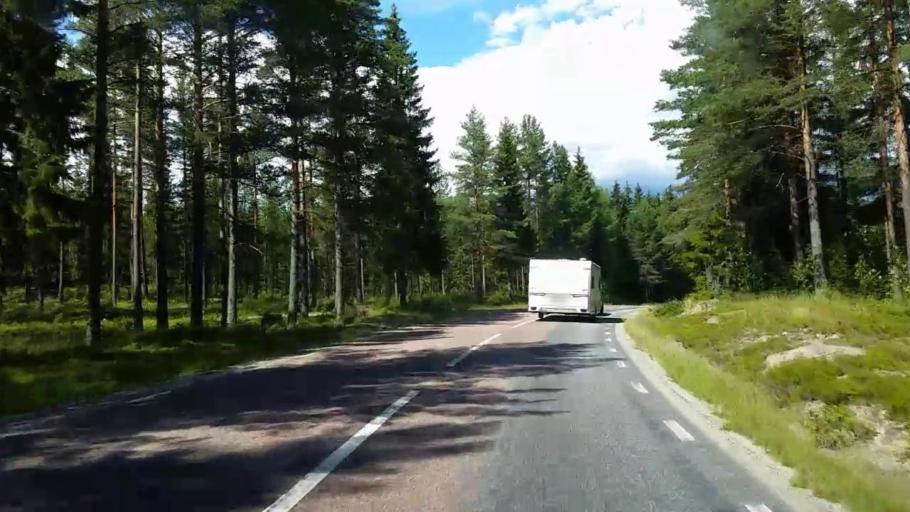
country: SE
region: Gaevleborg
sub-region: Ovanakers Kommun
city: Edsbyn
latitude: 61.3083
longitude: 15.5053
